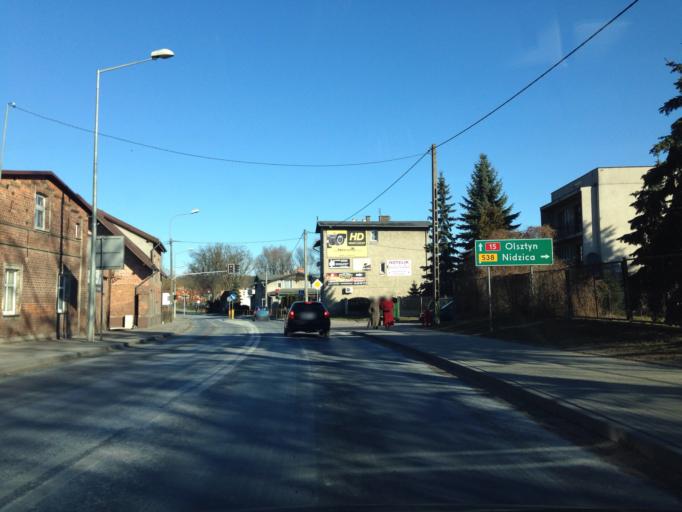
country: PL
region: Warmian-Masurian Voivodeship
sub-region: Powiat nowomiejski
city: Nowe Miasto Lubawskie
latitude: 53.4200
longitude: 19.5936
